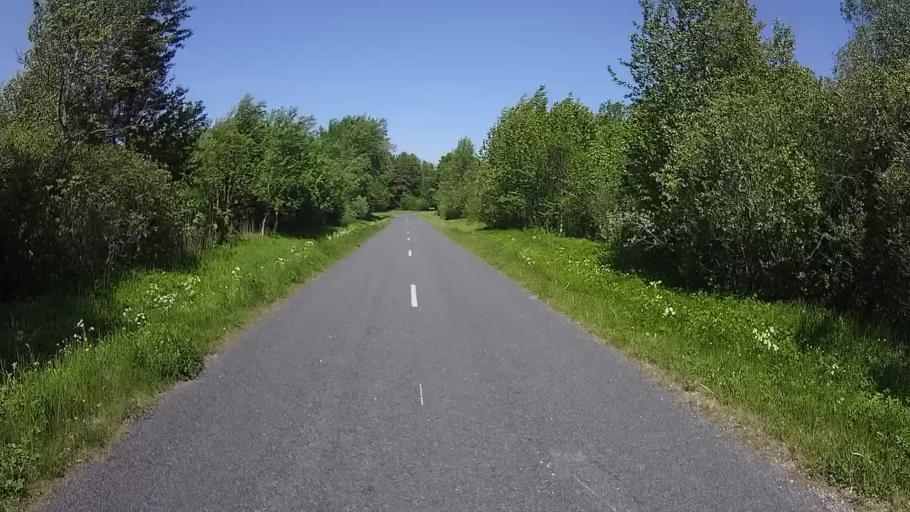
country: LV
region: Dundaga
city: Dundaga
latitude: 57.9402
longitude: 22.0893
